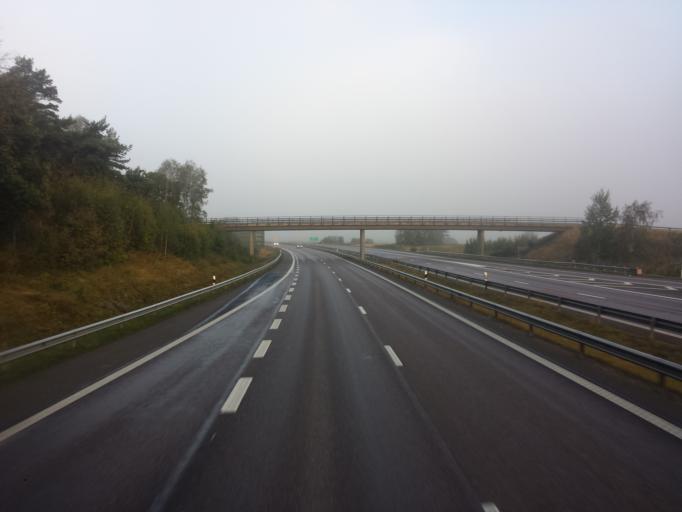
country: SE
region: Halland
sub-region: Kungsbacka Kommun
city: Fjaeras kyrkby
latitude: 57.4323
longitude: 12.1530
